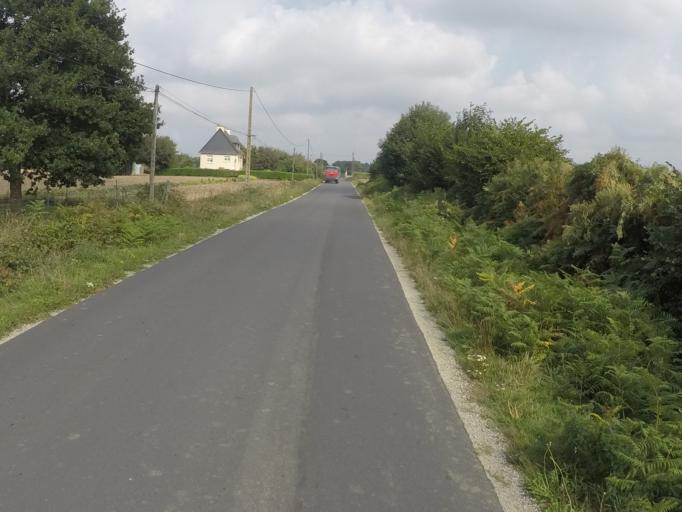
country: FR
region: Brittany
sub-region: Departement des Cotes-d'Armor
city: Lanrodec
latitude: 48.5420
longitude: -3.0332
